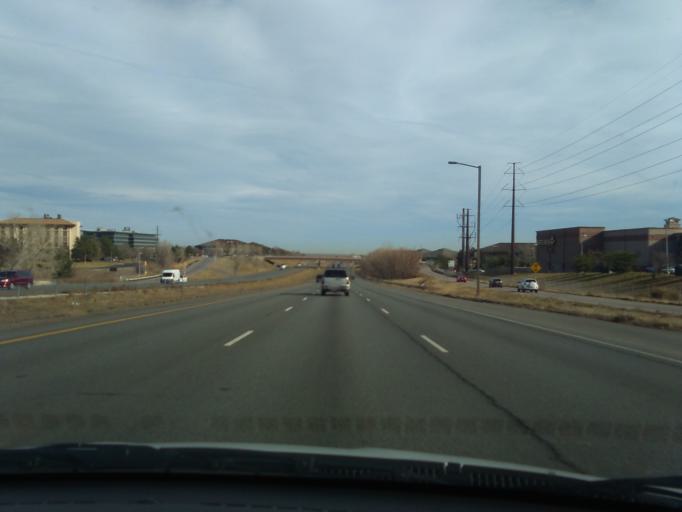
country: US
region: Colorado
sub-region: Jefferson County
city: West Pleasant View
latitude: 39.7367
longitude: -105.1630
